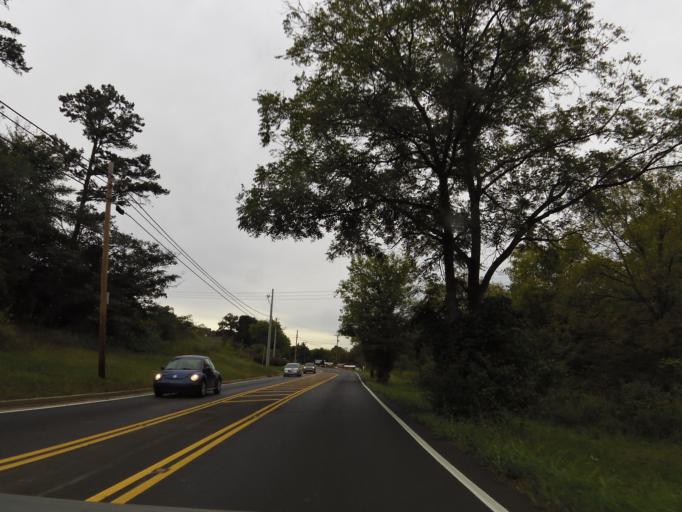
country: US
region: Tennessee
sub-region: Blount County
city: Louisville
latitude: 35.8791
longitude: -84.0411
